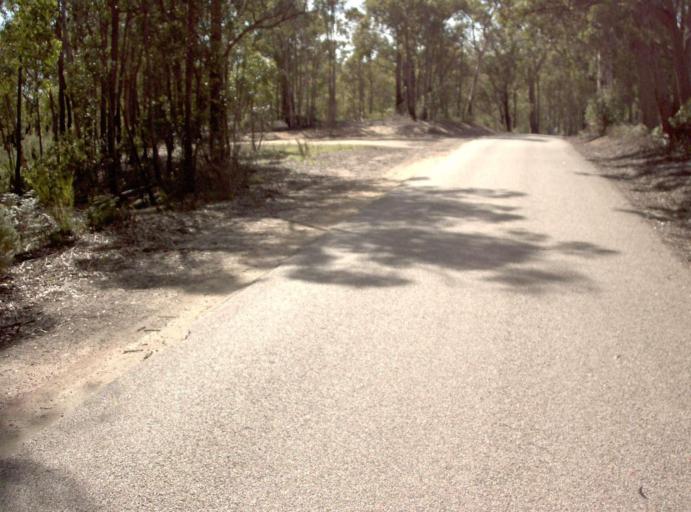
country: AU
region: Victoria
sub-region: East Gippsland
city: Lakes Entrance
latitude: -37.5248
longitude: 148.1535
